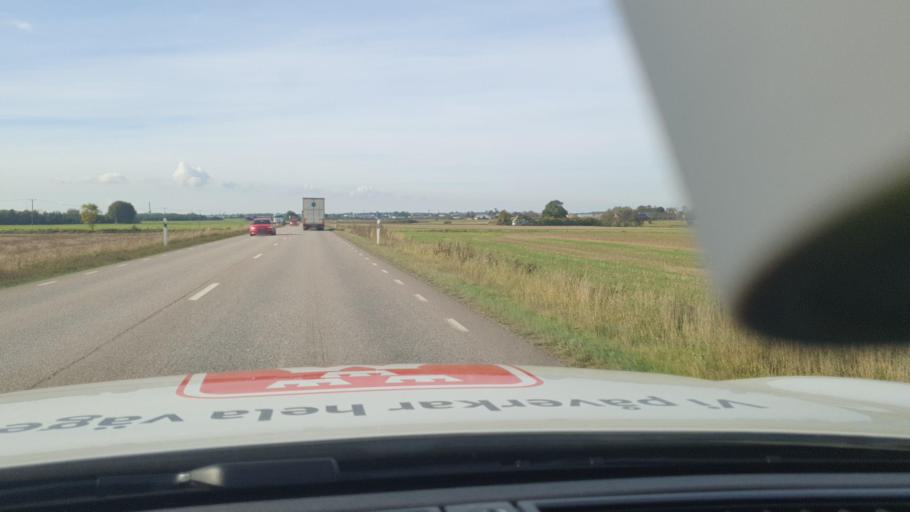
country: SE
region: Skane
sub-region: Angelholms Kommun
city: Munka-Ljungby
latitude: 56.2541
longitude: 12.9450
